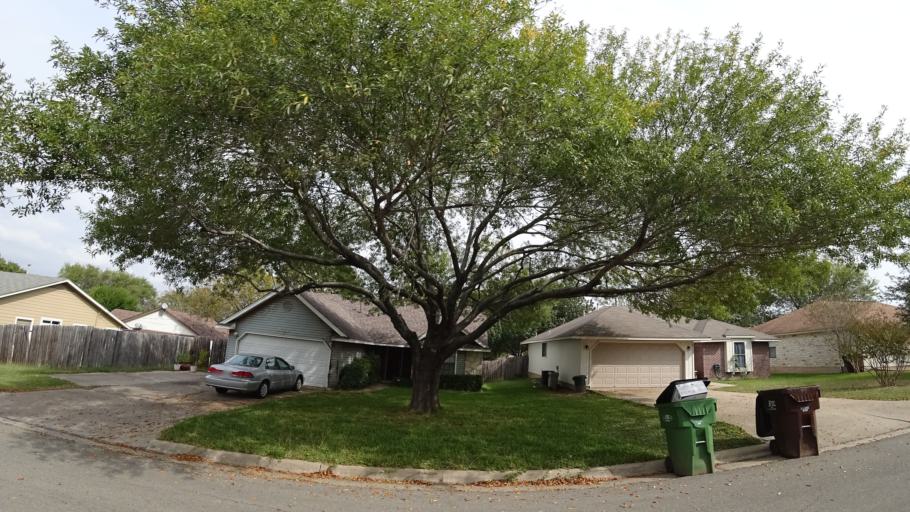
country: US
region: Texas
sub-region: Williamson County
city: Round Rock
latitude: 30.4897
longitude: -97.6838
